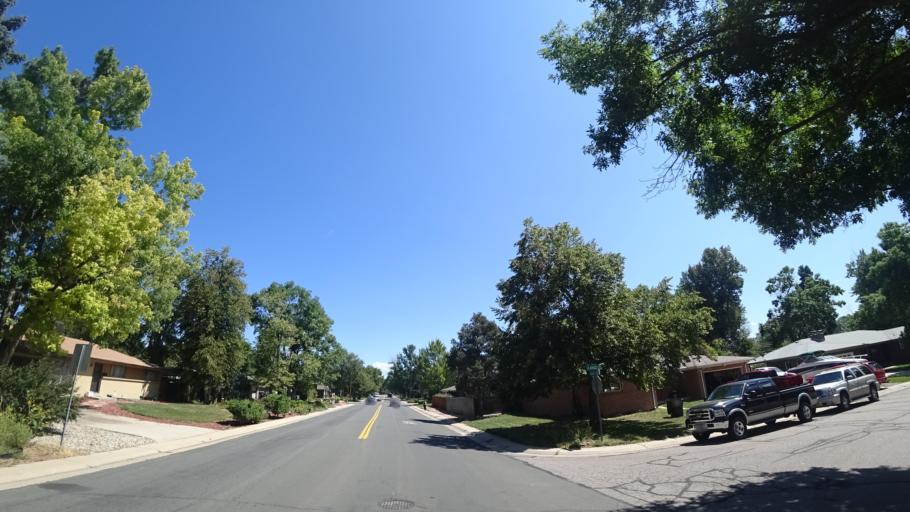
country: US
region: Colorado
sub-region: Arapahoe County
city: Littleton
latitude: 39.6021
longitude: -104.9960
